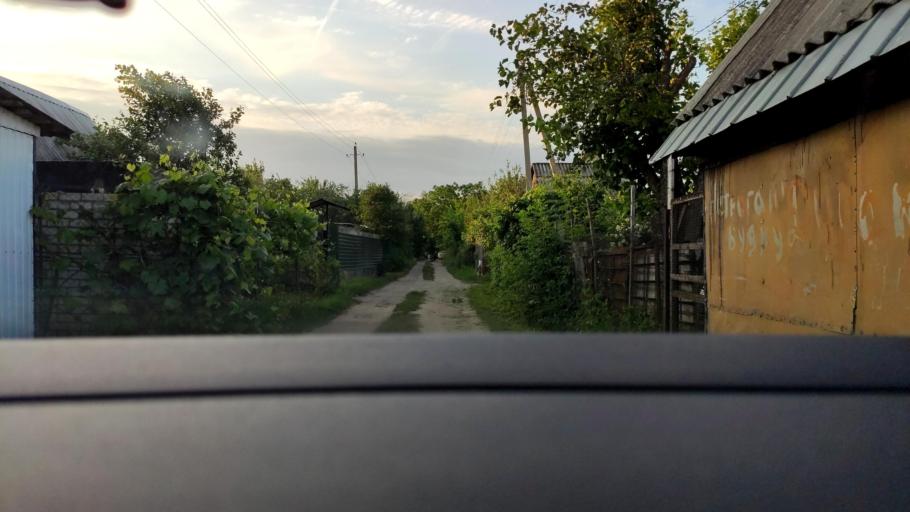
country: RU
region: Voronezj
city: Ramon'
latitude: 51.9121
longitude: 39.1753
